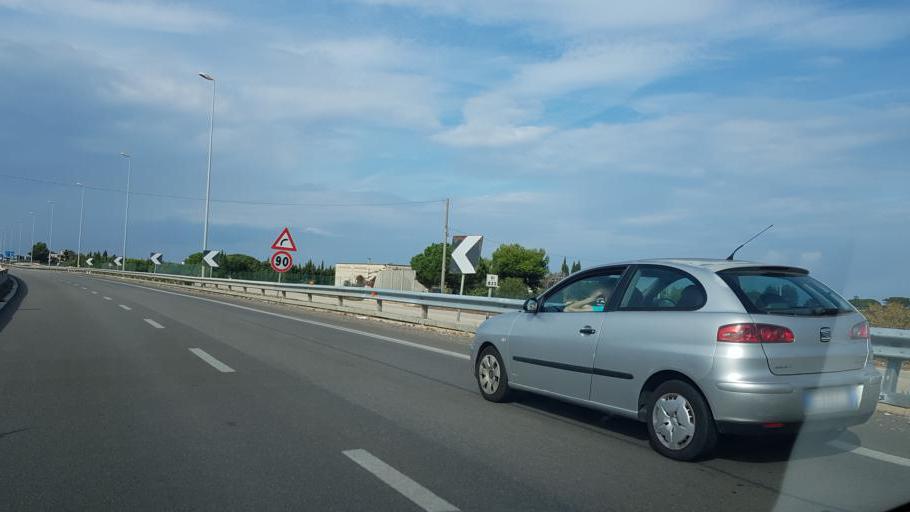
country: IT
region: Apulia
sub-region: Provincia di Bari
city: Polignano a Mare
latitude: 41.0055
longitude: 17.1958
